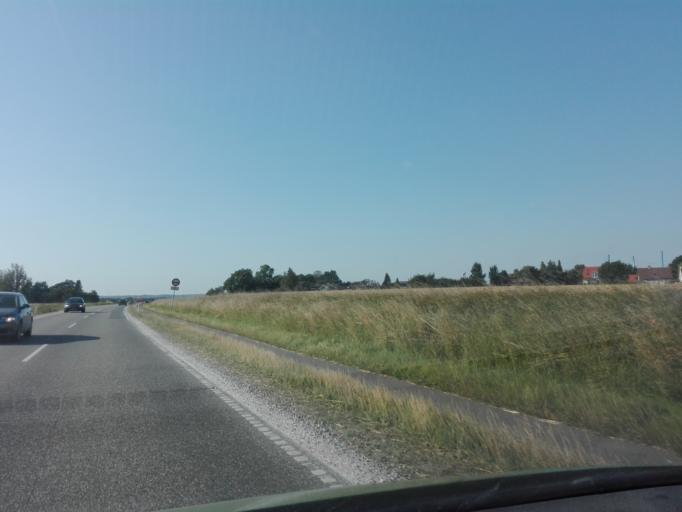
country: DK
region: Central Jutland
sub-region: Odder Kommune
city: Odder
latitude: 55.9385
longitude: 10.2152
